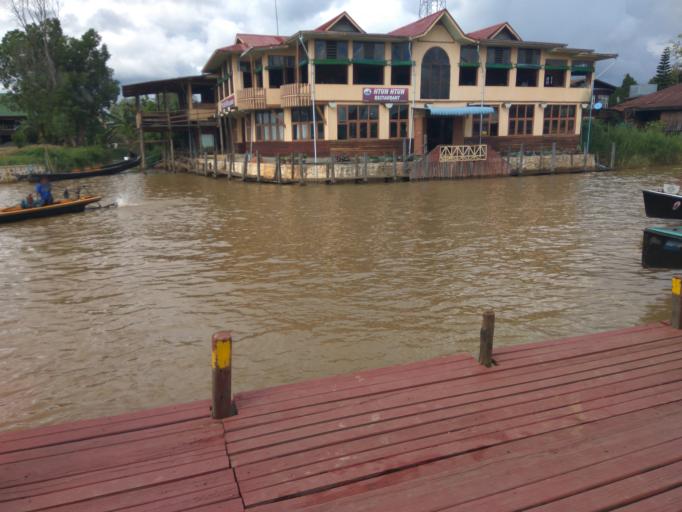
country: MM
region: Shan
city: Taunggyi
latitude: 20.4749
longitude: 96.8902
